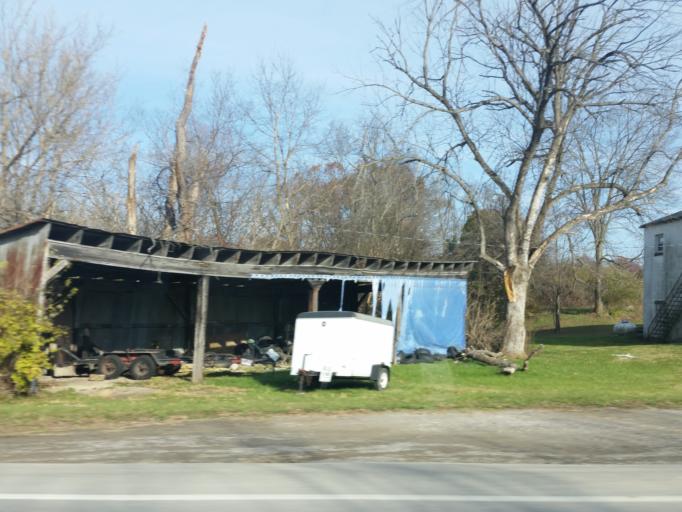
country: US
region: Kentucky
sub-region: Campbell County
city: Claryville
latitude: 38.8382
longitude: -84.3701
